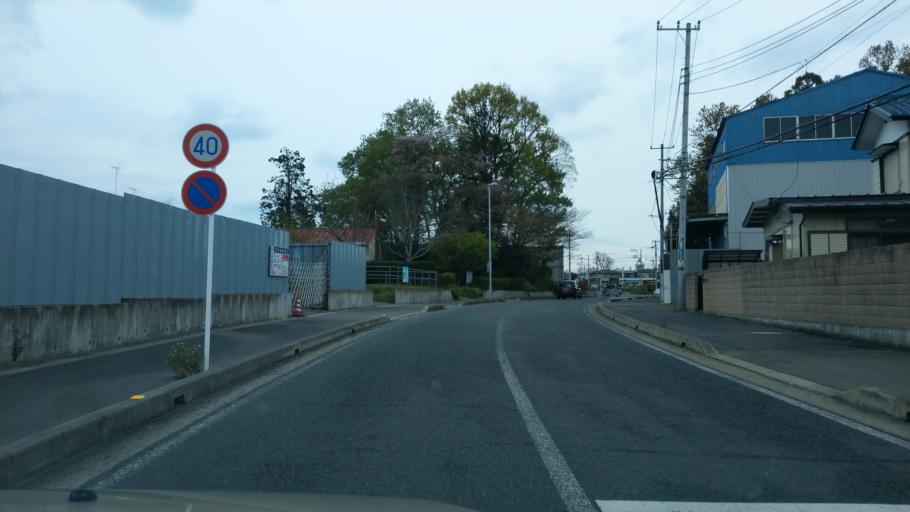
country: JP
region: Saitama
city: Ageoshimo
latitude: 35.9278
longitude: 139.5840
